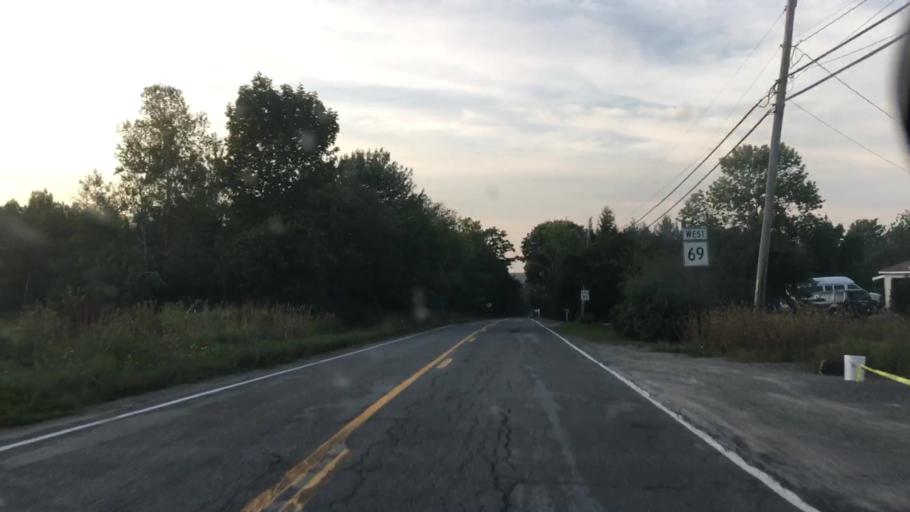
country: US
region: Maine
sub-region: Waldo County
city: Frankfort
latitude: 44.6987
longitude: -68.9446
